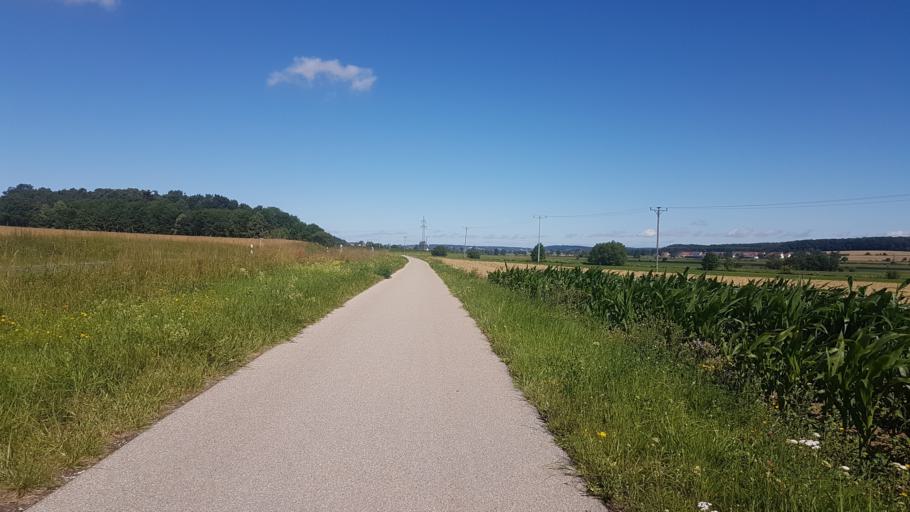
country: DE
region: Bavaria
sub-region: Regierungsbezirk Mittelfranken
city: Burgoberbach
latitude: 49.1948
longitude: 10.5670
